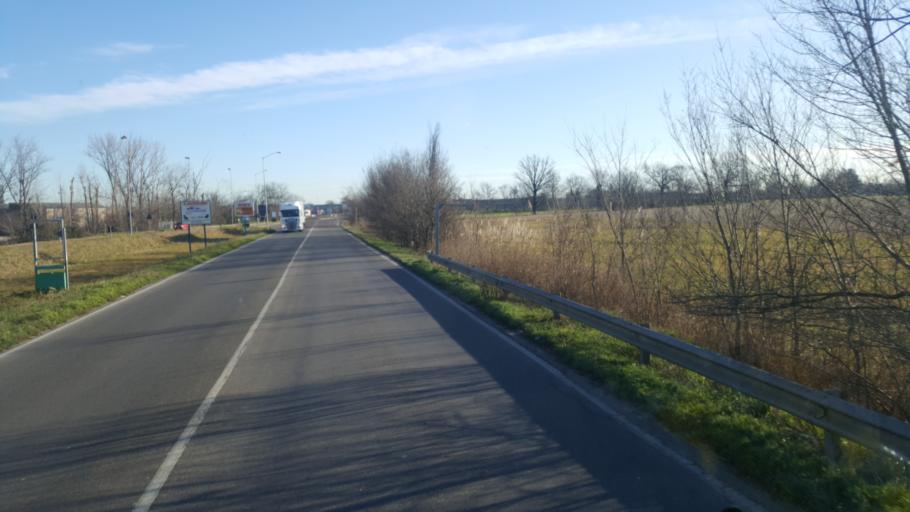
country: IT
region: Emilia-Romagna
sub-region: Provincia di Modena
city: Baggiovara
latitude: 44.6467
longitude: 10.8583
